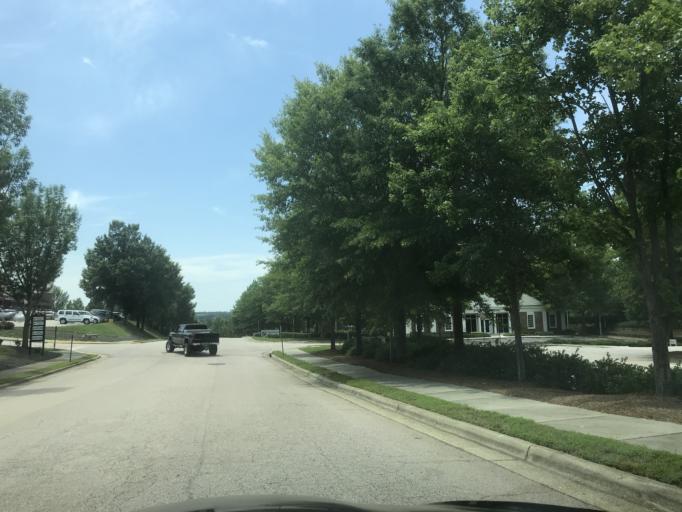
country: US
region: North Carolina
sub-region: Wake County
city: Wake Forest
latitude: 35.9447
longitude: -78.5427
